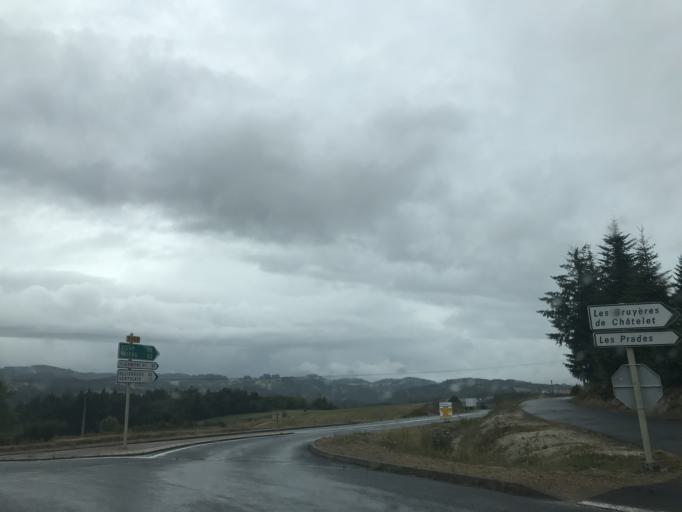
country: FR
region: Auvergne
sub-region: Departement du Puy-de-Dome
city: Ambert
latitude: 45.5744
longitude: 3.7475
